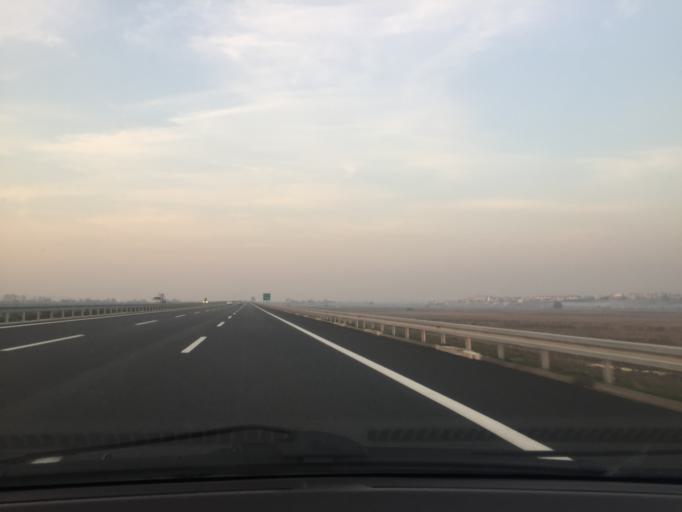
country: TR
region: Bursa
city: Karacabey
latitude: 40.2121
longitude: 28.3887
